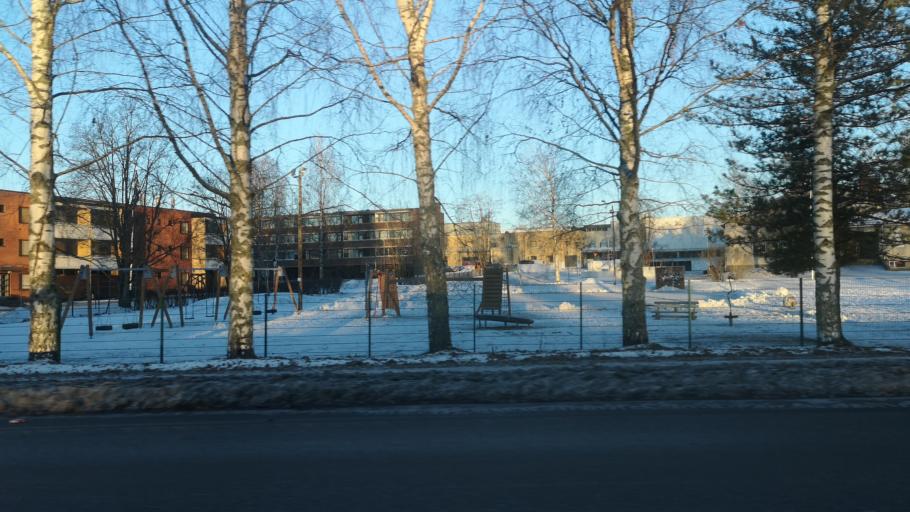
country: FI
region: Southern Savonia
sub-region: Pieksaemaeki
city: Juva
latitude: 61.8957
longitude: 27.8557
